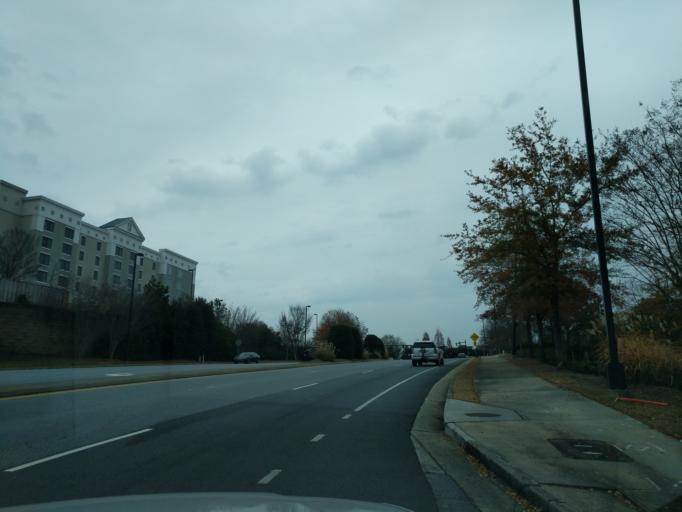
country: US
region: Georgia
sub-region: Fulton County
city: Alpharetta
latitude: 34.0486
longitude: -84.2832
